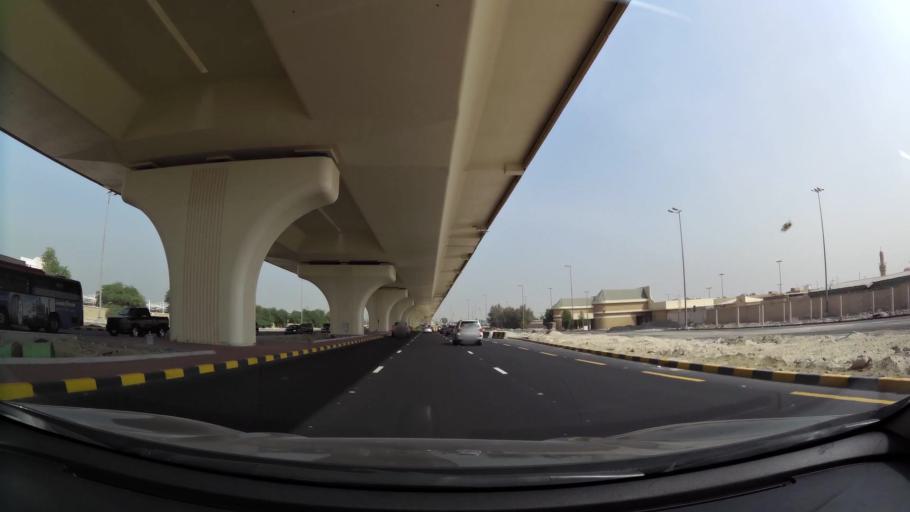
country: KW
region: Al Asimah
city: Ar Rabiyah
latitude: 29.3253
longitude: 47.9168
